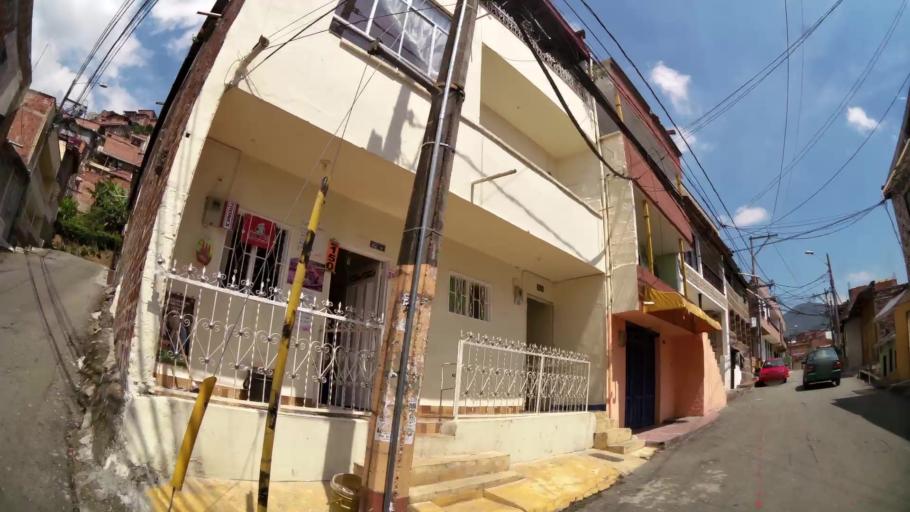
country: CO
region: Antioquia
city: La Estrella
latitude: 6.1836
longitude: -75.6595
